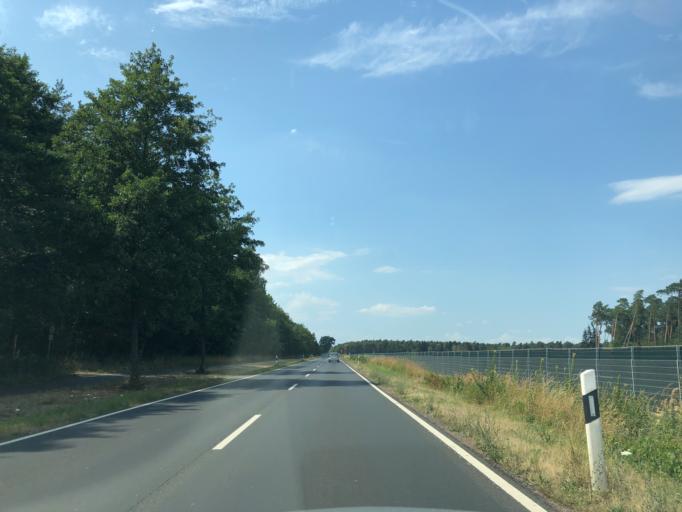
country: DE
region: Hesse
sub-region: Regierungsbezirk Darmstadt
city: Babenhausen
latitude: 49.9896
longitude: 8.9133
